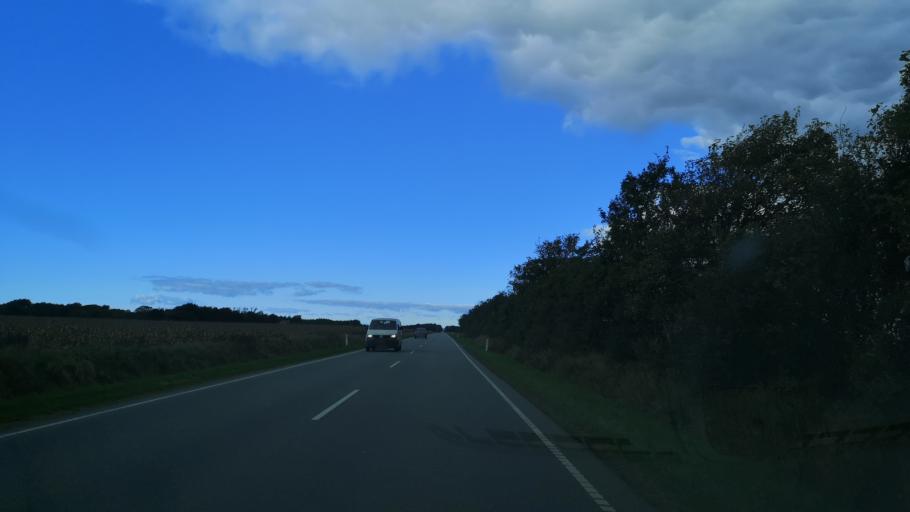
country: DK
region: South Denmark
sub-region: Tonder Kommune
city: Sherrebek
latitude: 55.0848
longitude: 8.8226
